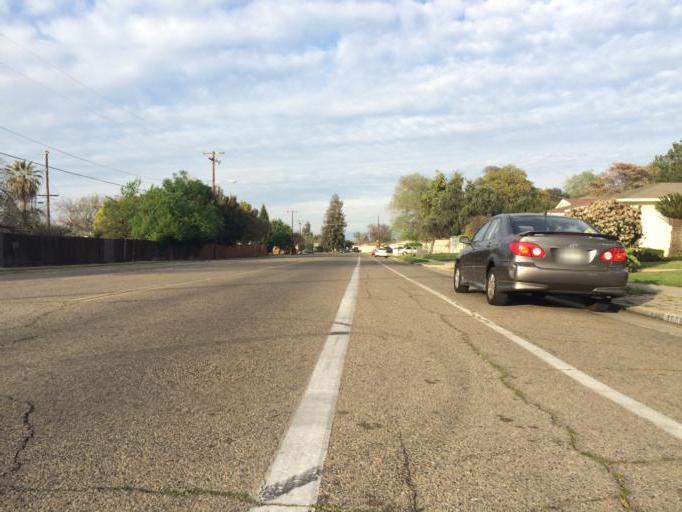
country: US
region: California
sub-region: Fresno County
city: Fresno
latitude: 36.8028
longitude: -119.7626
